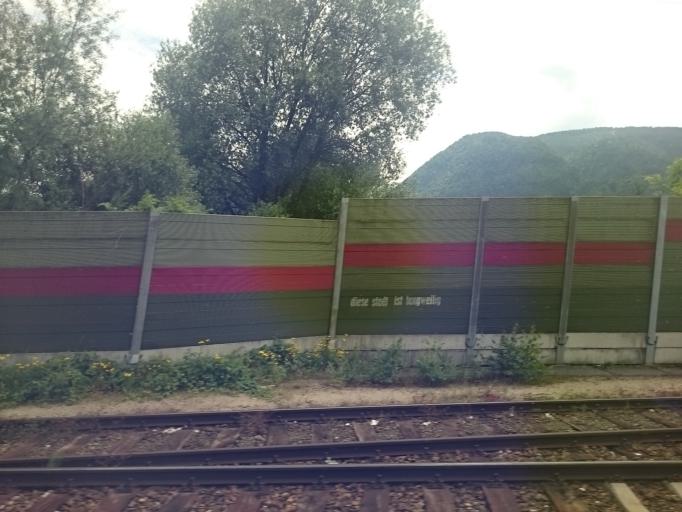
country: AT
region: Tyrol
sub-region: Politischer Bezirk Kufstein
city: Worgl
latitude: 47.4895
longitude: 12.0569
